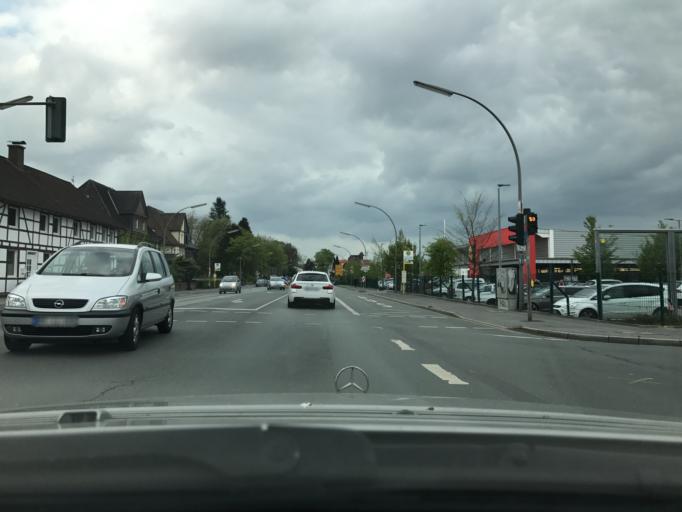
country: DE
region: North Rhine-Westphalia
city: Waltrop
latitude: 51.6183
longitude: 7.3934
